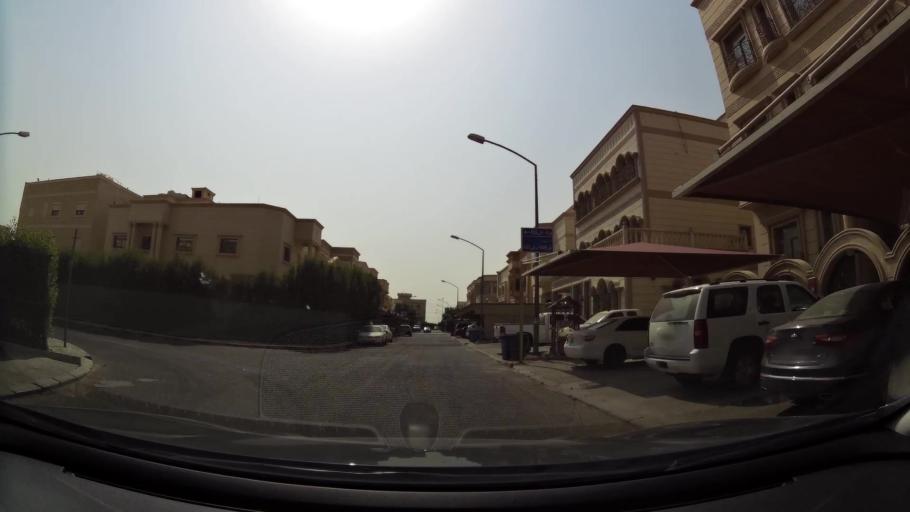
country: KW
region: Muhafazat al Jahra'
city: Al Jahra'
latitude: 29.3021
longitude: 47.7196
